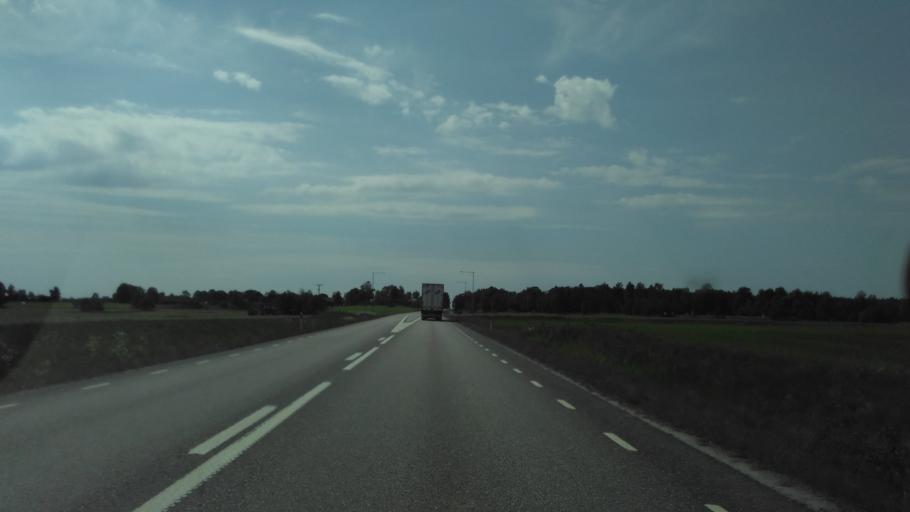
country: SE
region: Vaestra Goetaland
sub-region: Grastorps Kommun
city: Graestorp
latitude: 58.4049
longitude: 12.8246
